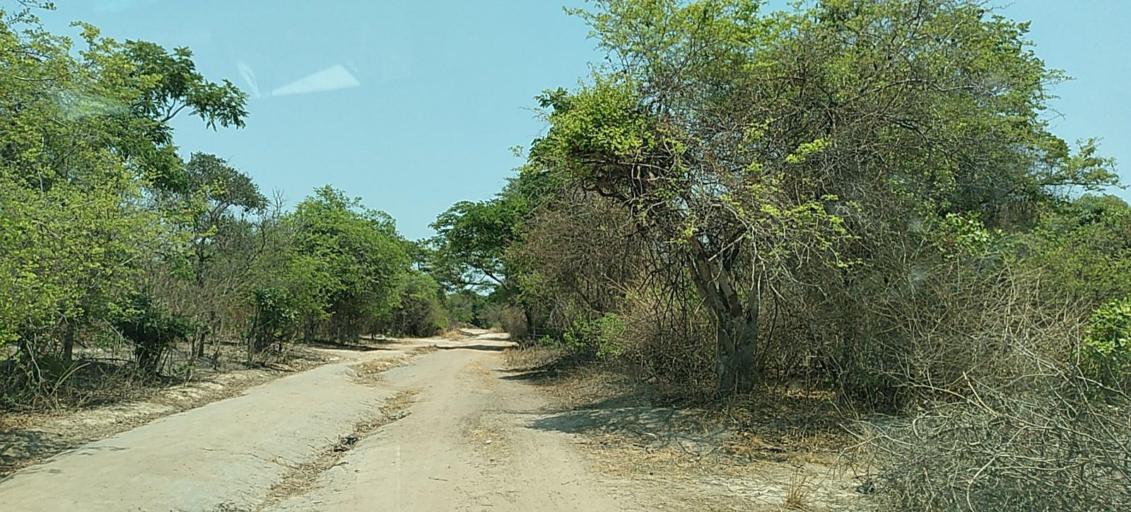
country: ZM
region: Copperbelt
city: Mpongwe
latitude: -13.8670
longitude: 27.8814
